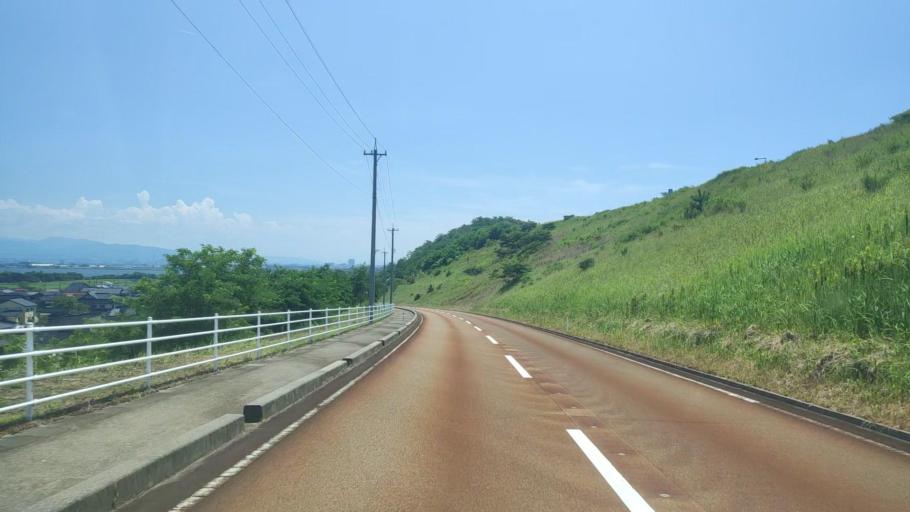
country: JP
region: Ishikawa
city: Kanazawa-shi
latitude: 36.6693
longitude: 136.6581
